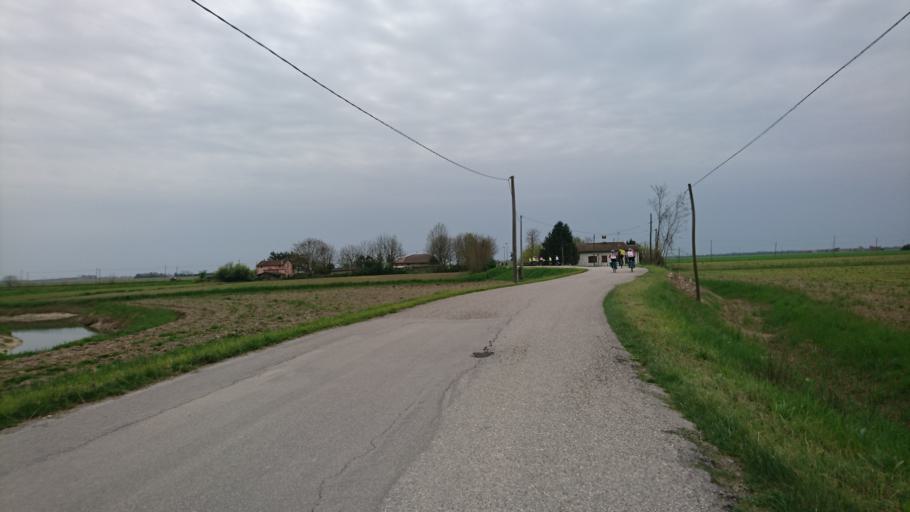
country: IT
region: Veneto
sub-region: Provincia di Venezia
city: Lugugnana
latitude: 45.6988
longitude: 12.9203
